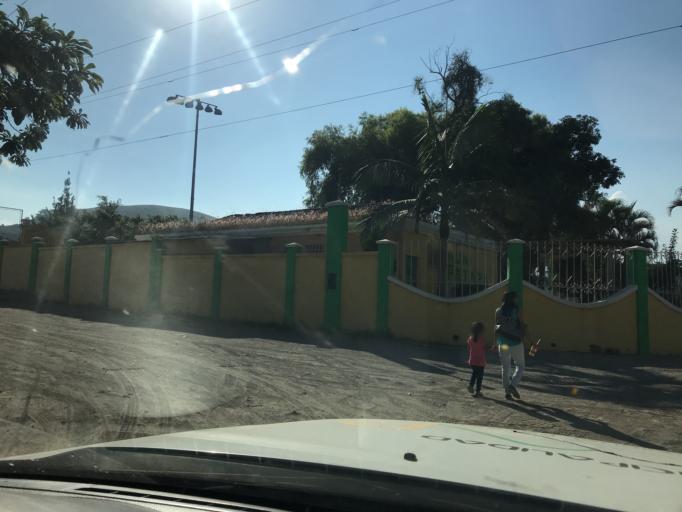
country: GT
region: Guatemala
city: Petapa
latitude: 14.4940
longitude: -90.5572
